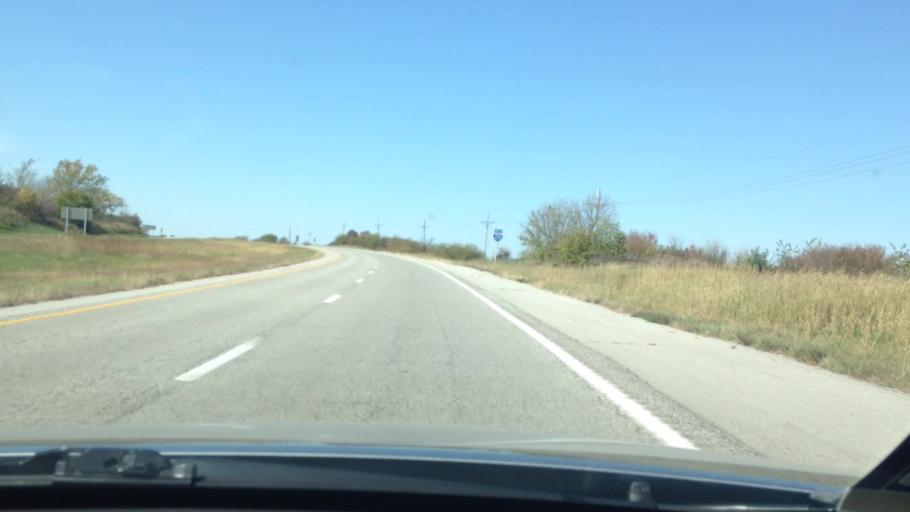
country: US
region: Missouri
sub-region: Platte County
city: Weatherby Lake
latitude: 39.3149
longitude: -94.6775
